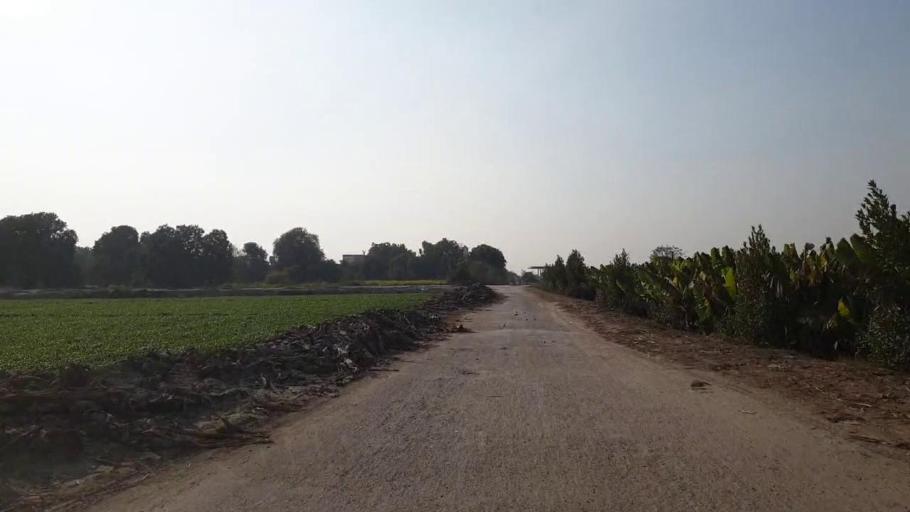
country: PK
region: Sindh
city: Matiari
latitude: 25.5995
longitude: 68.6041
